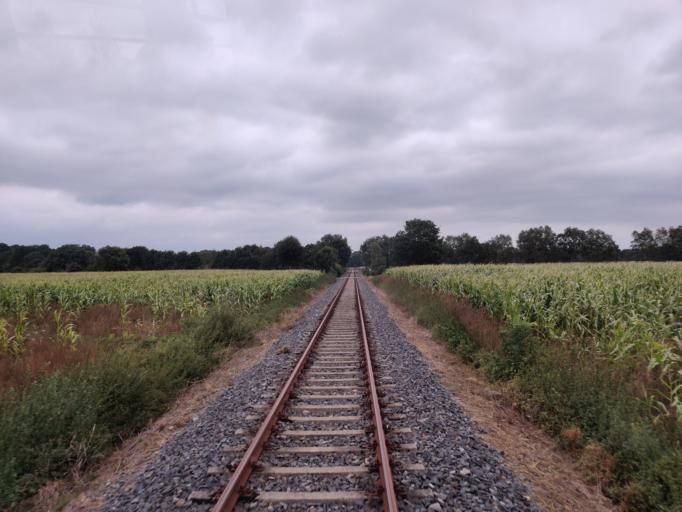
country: DE
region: Lower Saxony
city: Vollersode
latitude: 53.2877
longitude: 8.9693
